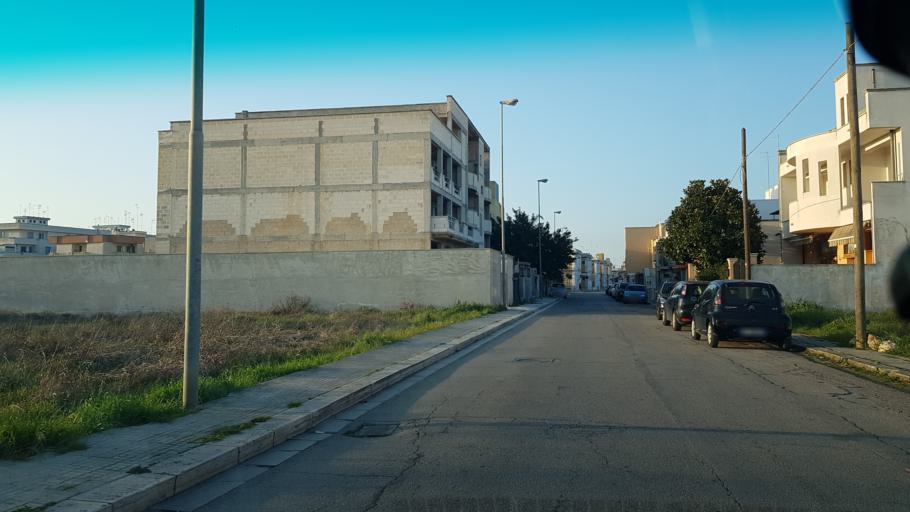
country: IT
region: Apulia
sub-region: Provincia di Brindisi
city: Mesagne
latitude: 40.5564
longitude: 17.7987
